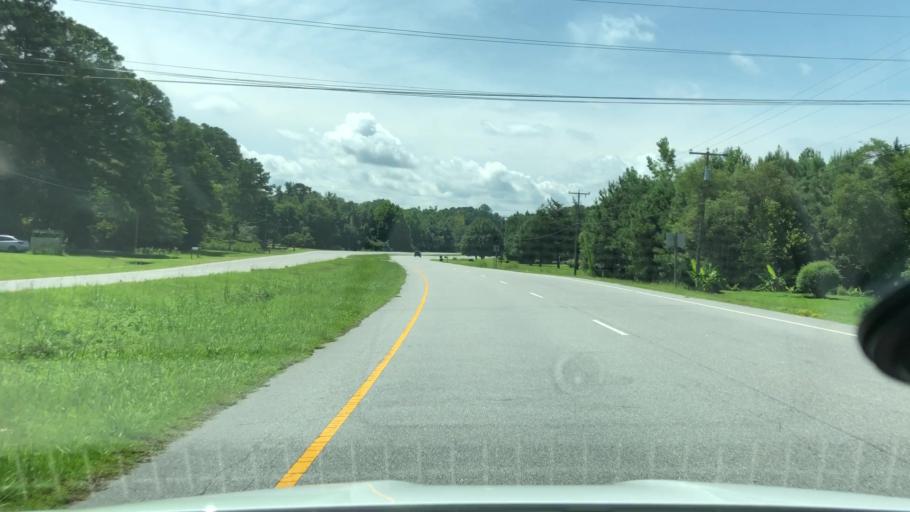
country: US
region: North Carolina
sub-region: Martin County
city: Williamston
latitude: 35.7931
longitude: -77.0600
